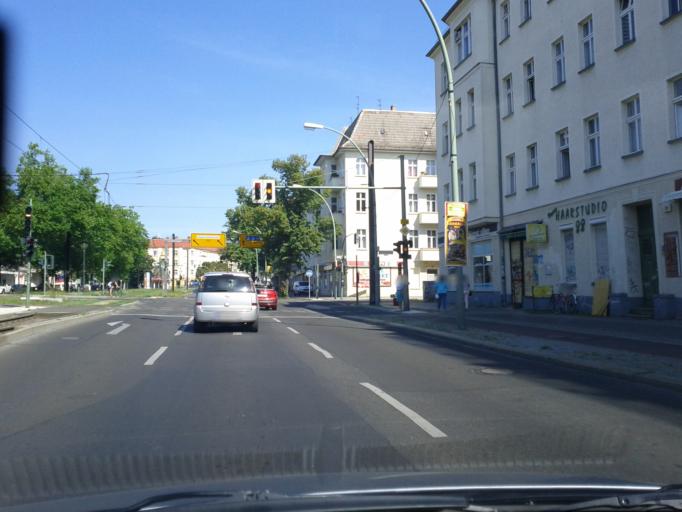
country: DE
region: Berlin
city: Pankow
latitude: 52.5574
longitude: 13.4144
